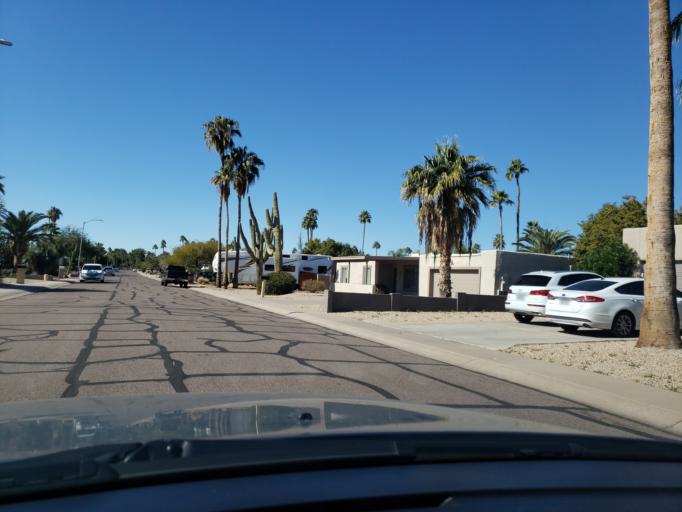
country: US
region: Arizona
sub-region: Maricopa County
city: Paradise Valley
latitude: 33.6127
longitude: -111.9307
